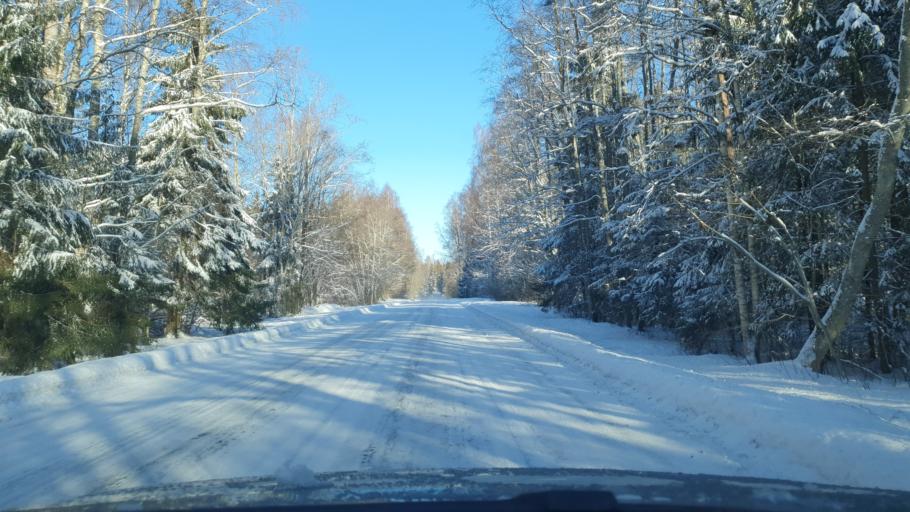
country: EE
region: Harju
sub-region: Kuusalu vald
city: Kuusalu
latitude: 59.5524
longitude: 25.5589
